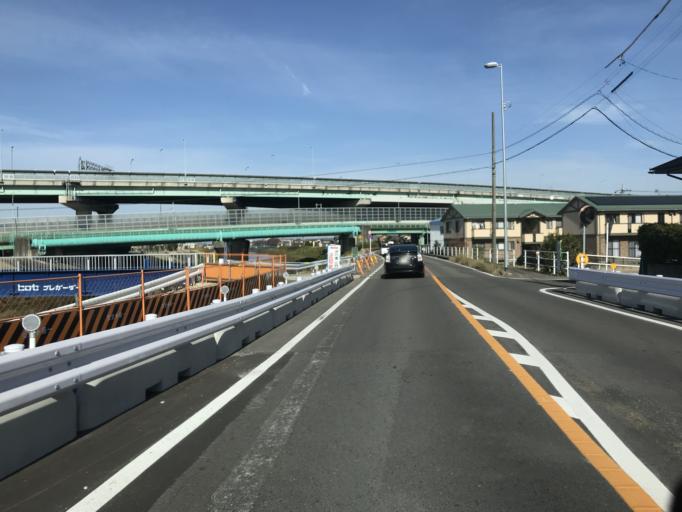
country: JP
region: Aichi
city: Iwakura
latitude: 35.2192
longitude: 136.8446
